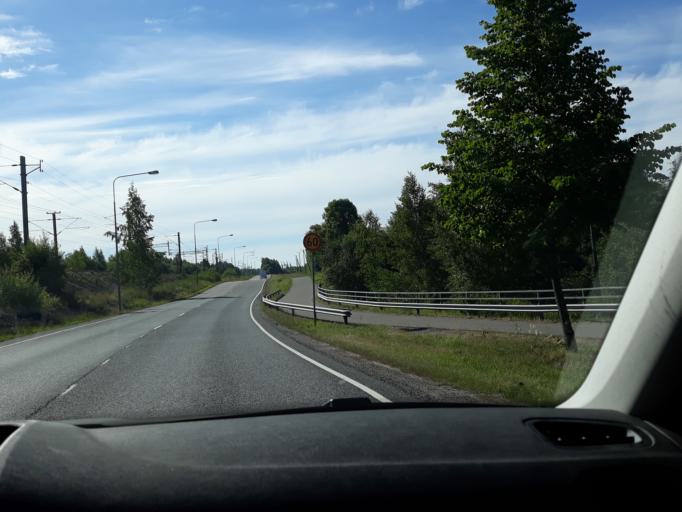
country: FI
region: Uusimaa
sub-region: Helsinki
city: Jaervenpaeae
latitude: 60.5491
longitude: 24.9777
